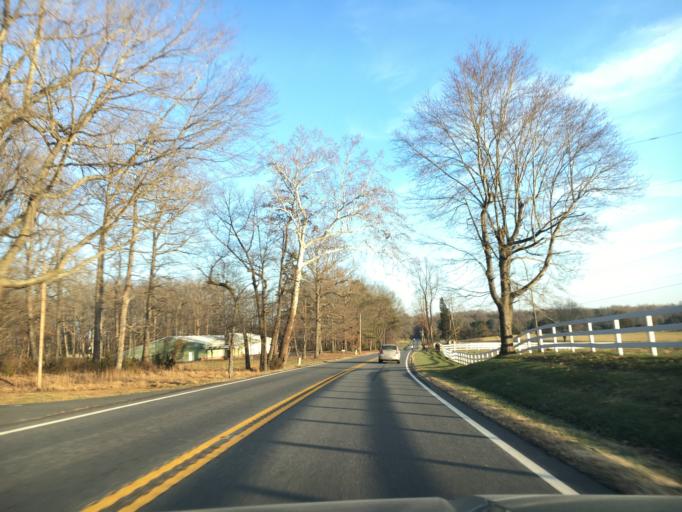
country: US
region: Virginia
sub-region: Culpeper County
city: Merrimac
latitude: 38.5220
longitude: -78.0915
